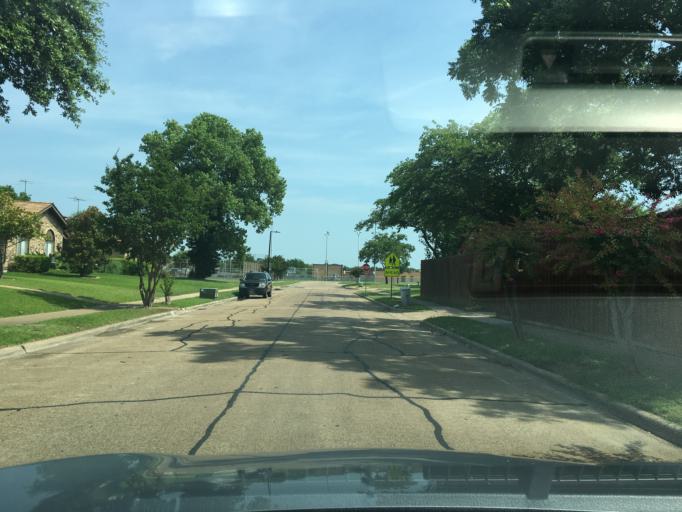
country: US
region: Texas
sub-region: Dallas County
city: Garland
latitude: 32.9252
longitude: -96.6763
